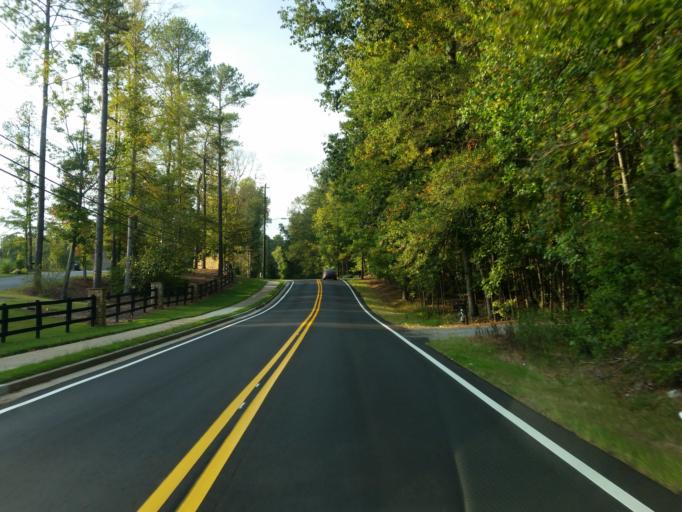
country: US
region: Georgia
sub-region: Cobb County
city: Marietta
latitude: 33.9878
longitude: -84.4595
